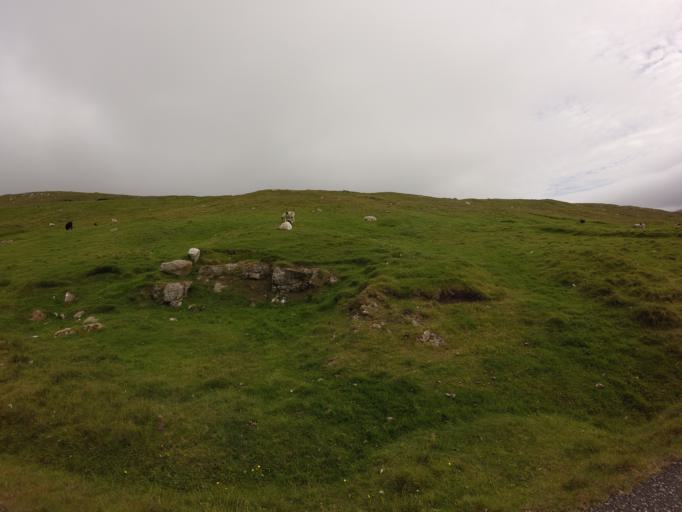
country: FO
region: Sandoy
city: Sandur
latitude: 61.8293
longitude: -6.7645
